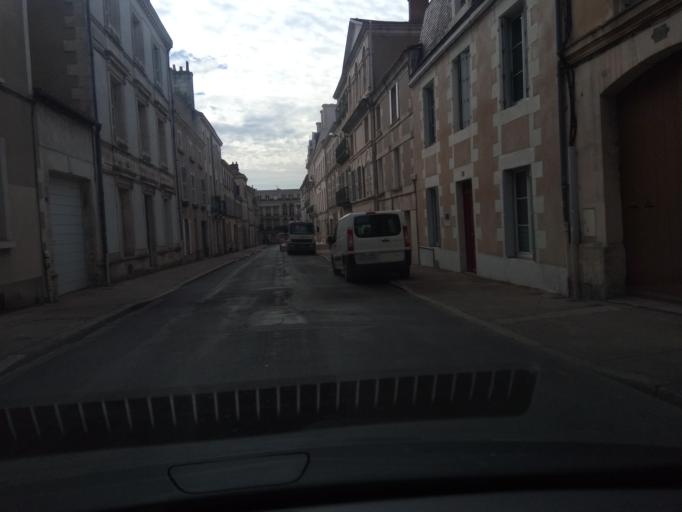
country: FR
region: Poitou-Charentes
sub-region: Departement de la Vienne
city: Poitiers
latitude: 46.5777
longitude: 0.3360
